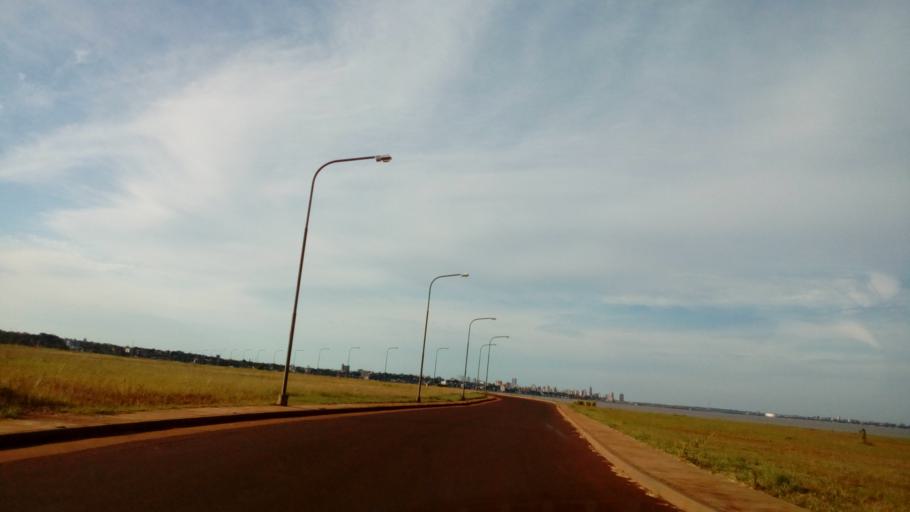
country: AR
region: Misiones
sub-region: Departamento de Capital
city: Posadas
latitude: -27.4174
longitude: -55.8812
